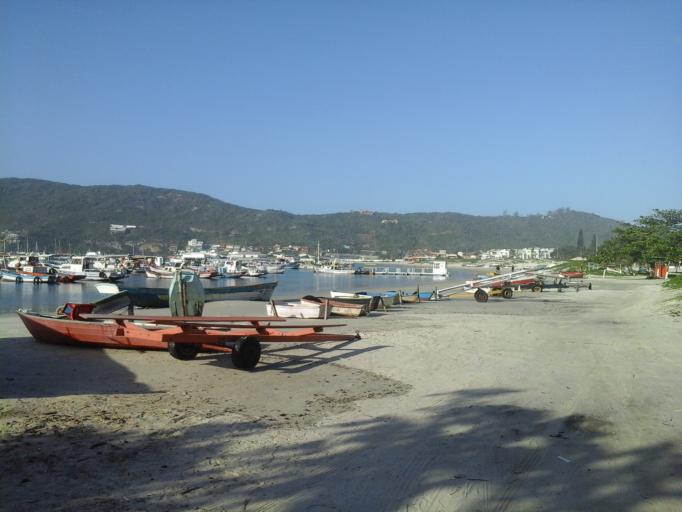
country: BR
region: Rio de Janeiro
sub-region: Arraial Do Cabo
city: Arraial do Cabo
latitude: -22.9699
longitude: -42.0190
